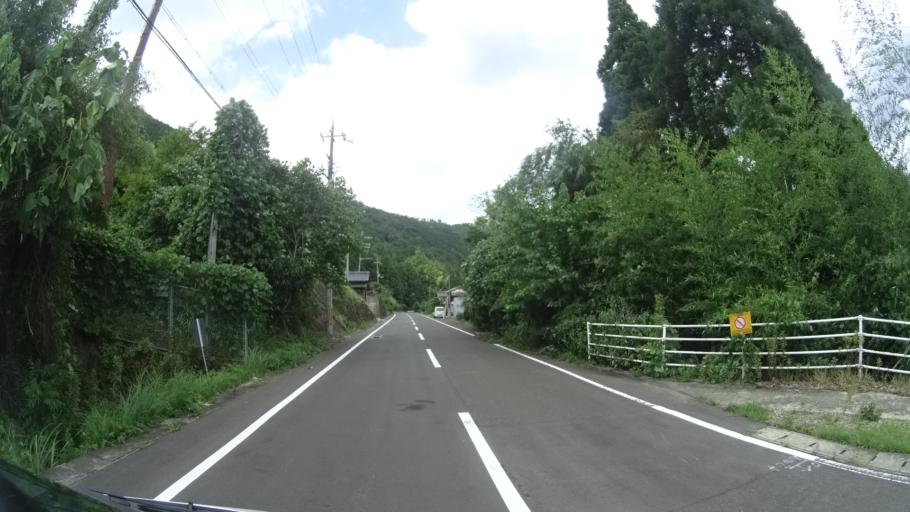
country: JP
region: Kyoto
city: Ayabe
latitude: 35.2754
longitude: 135.3329
